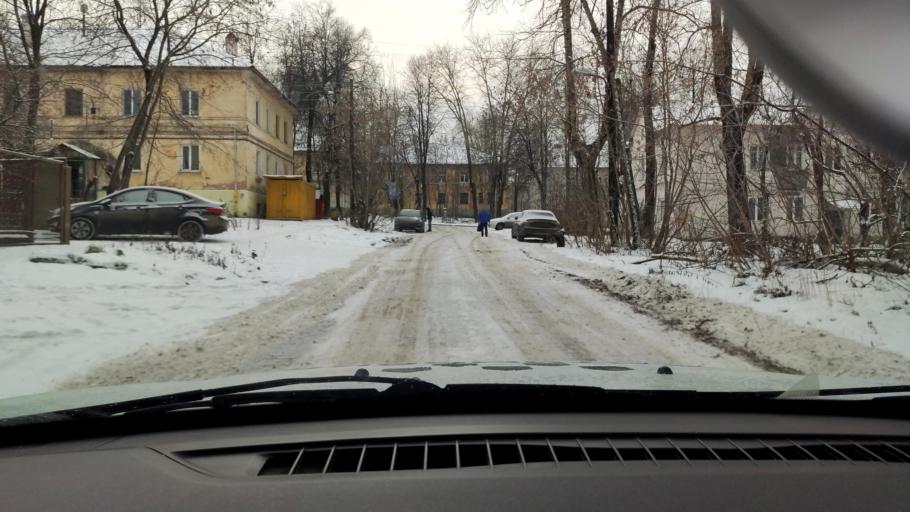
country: RU
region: Perm
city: Polazna
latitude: 58.1275
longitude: 56.3778
